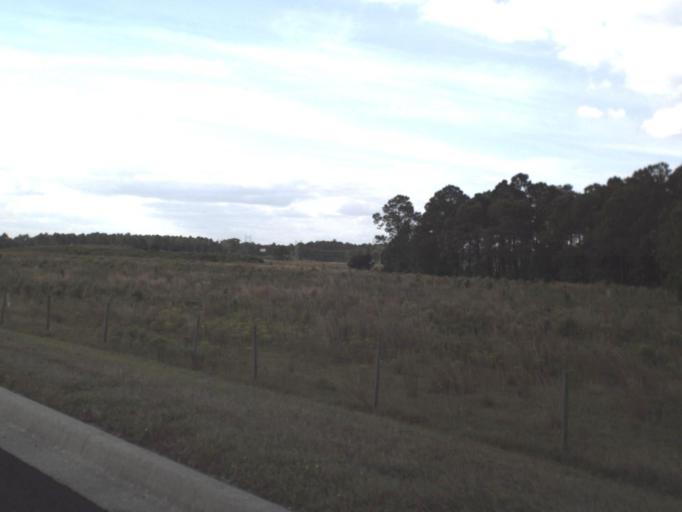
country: US
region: Florida
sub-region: Orange County
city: Hunters Creek
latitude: 28.3439
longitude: -81.4728
